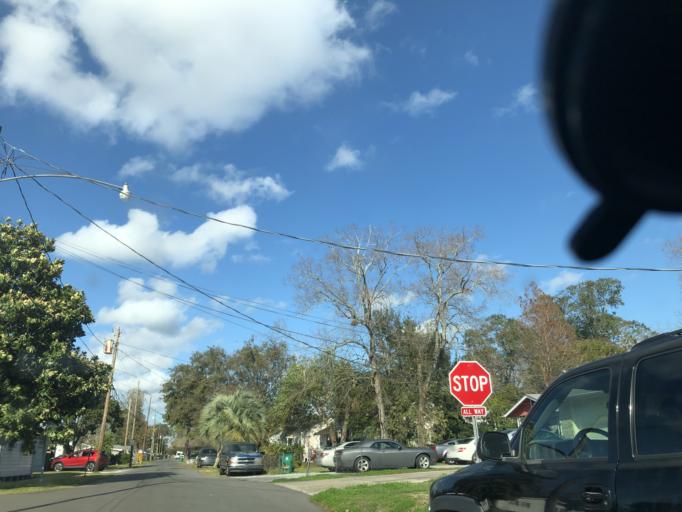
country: US
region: Louisiana
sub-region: Jefferson Parish
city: Metairie
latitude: 29.9836
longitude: -90.1590
